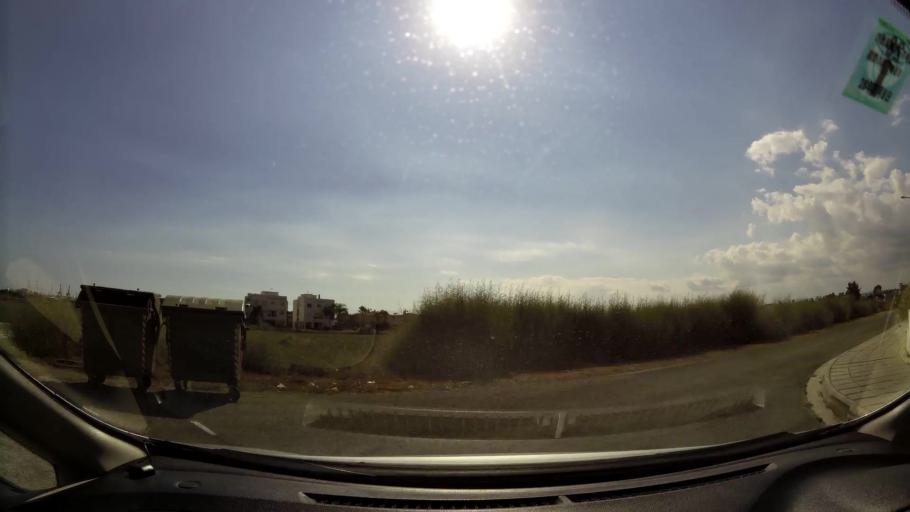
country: CY
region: Larnaka
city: Livadia
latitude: 34.9468
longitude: 33.6372
